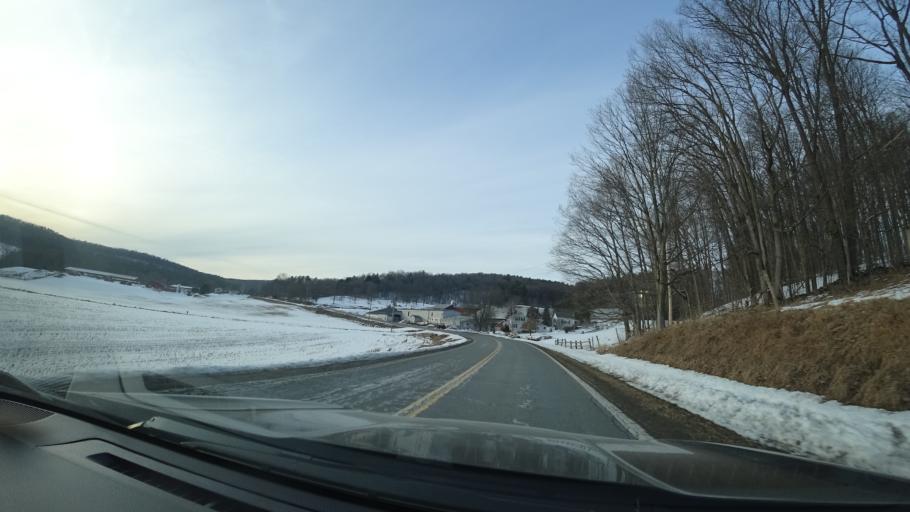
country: US
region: New York
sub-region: Washington County
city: Cambridge
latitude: 43.1878
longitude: -73.3710
